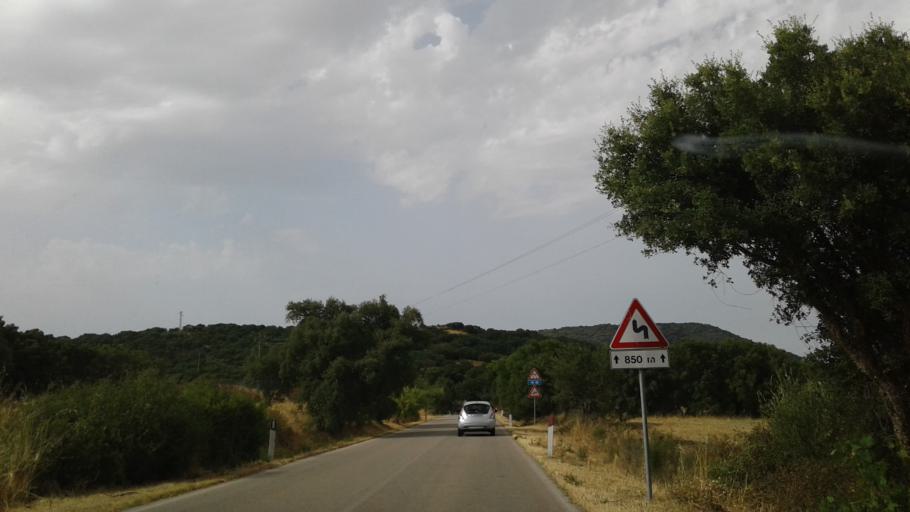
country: IT
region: Sardinia
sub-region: Provincia di Olbia-Tempio
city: Sant'Antonio di Gallura
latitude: 40.9575
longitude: 9.2946
